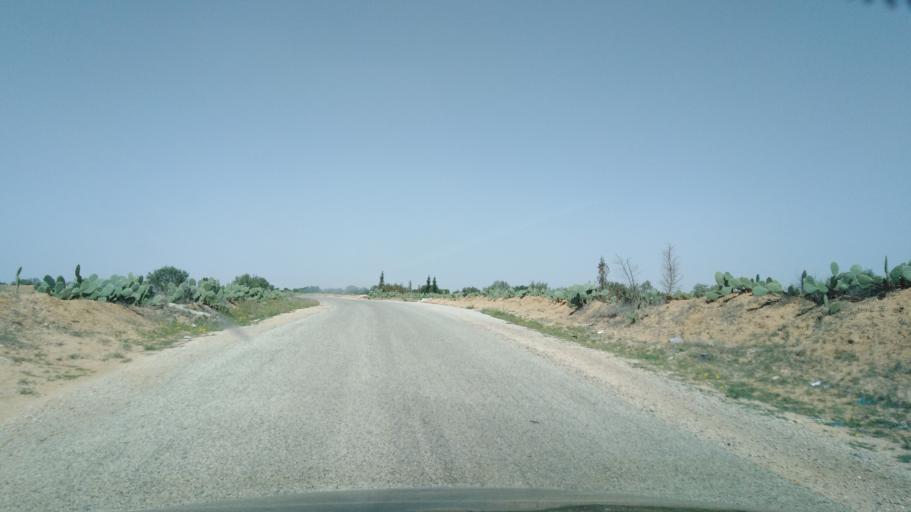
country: TN
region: Safaqis
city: Bi'r `Ali Bin Khalifah
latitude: 34.6788
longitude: 10.4126
